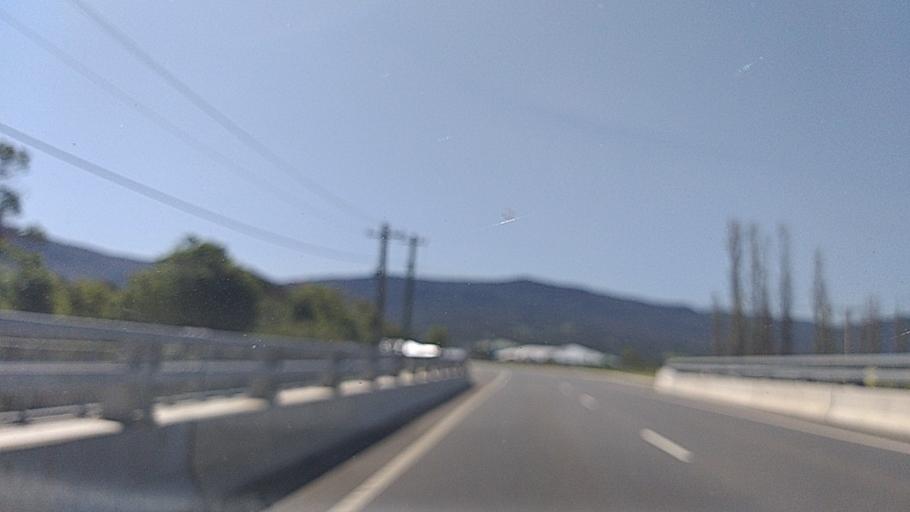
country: AU
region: New South Wales
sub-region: Wollongong
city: Dapto
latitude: -34.4844
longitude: 150.7676
